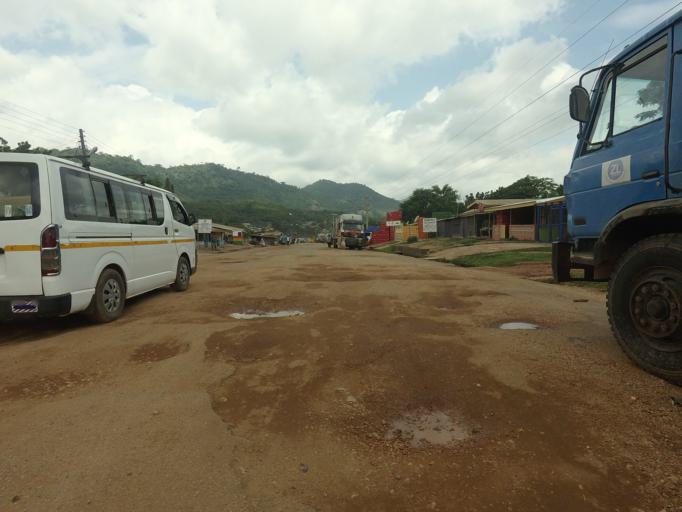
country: GH
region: Volta
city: Ho
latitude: 6.6871
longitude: 0.3331
